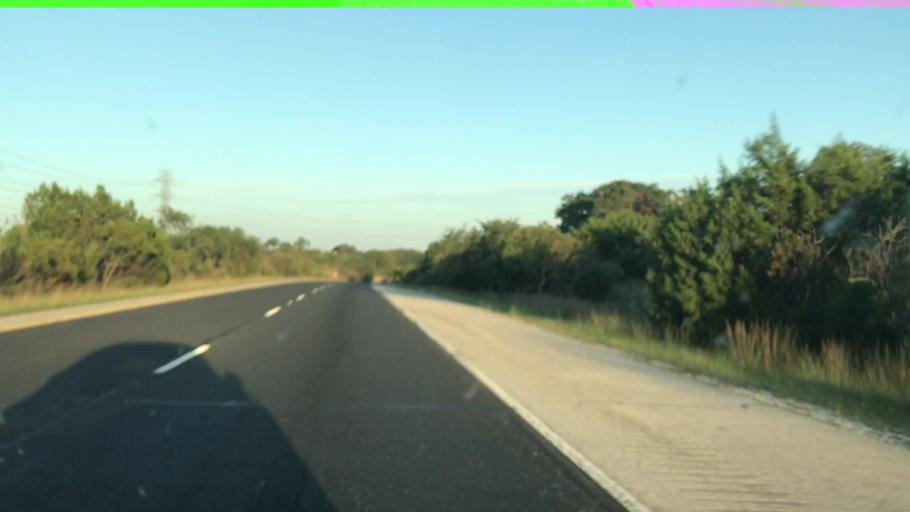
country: US
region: Texas
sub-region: Kerr County
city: Kerrville
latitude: 30.0677
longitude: -99.0592
